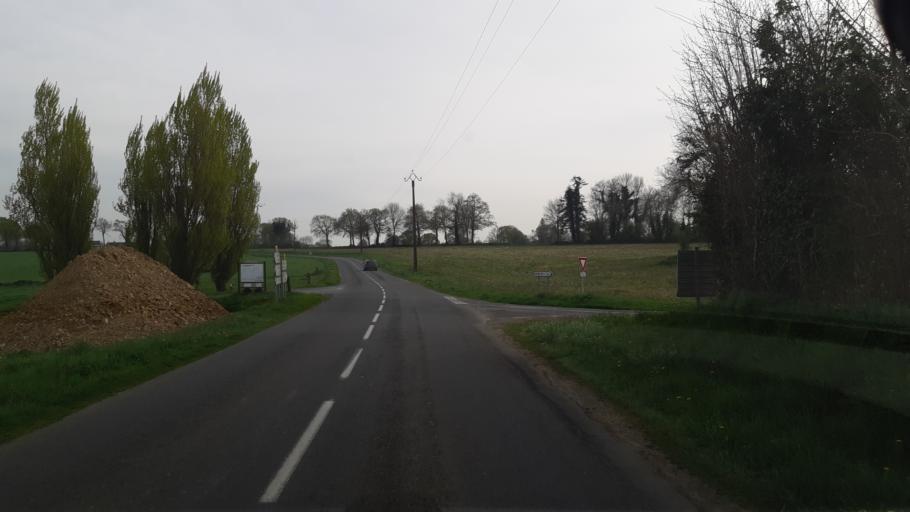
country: FR
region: Lower Normandy
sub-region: Departement de la Manche
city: Gavray
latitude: 48.9482
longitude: -1.3308
